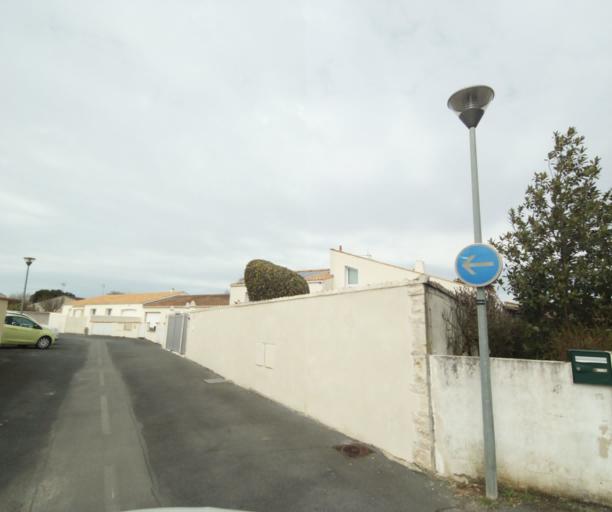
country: FR
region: Poitou-Charentes
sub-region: Departement de la Charente-Maritime
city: Lagord
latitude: 46.1842
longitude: -1.1596
